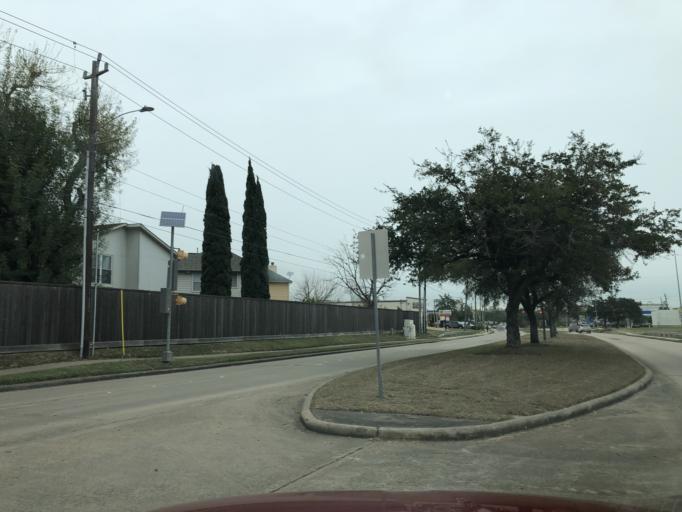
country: US
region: Texas
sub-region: Fort Bend County
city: Missouri City
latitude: 29.6399
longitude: -95.5286
